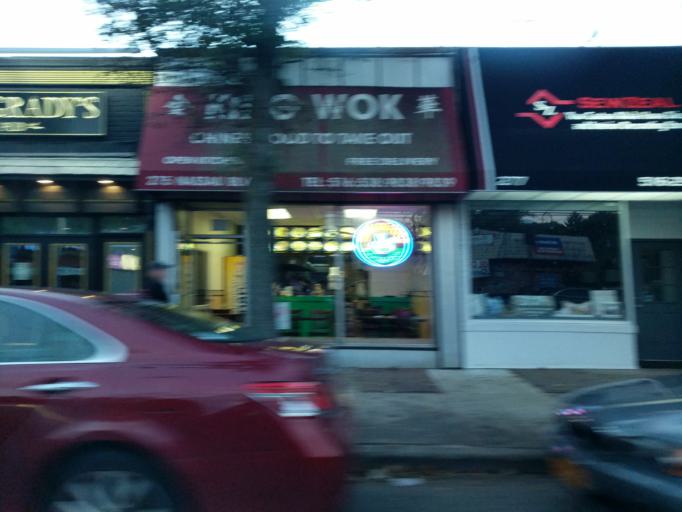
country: US
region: New York
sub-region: Nassau County
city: Garden City South
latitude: 40.7145
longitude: -73.6609
